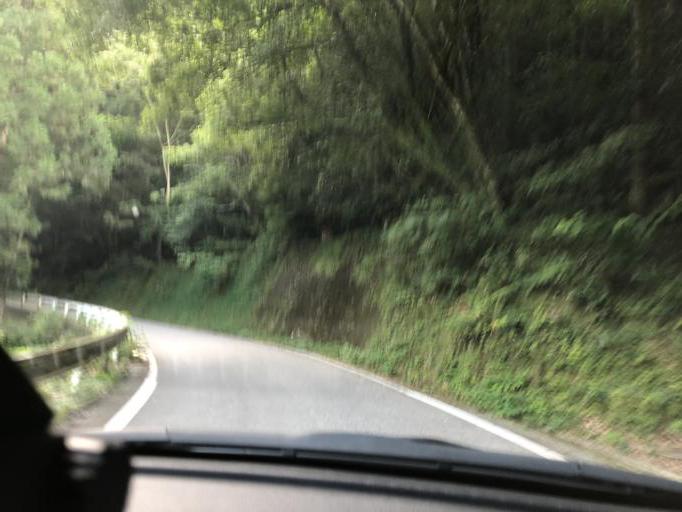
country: JP
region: Kochi
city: Kochi-shi
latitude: 33.6215
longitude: 133.4962
